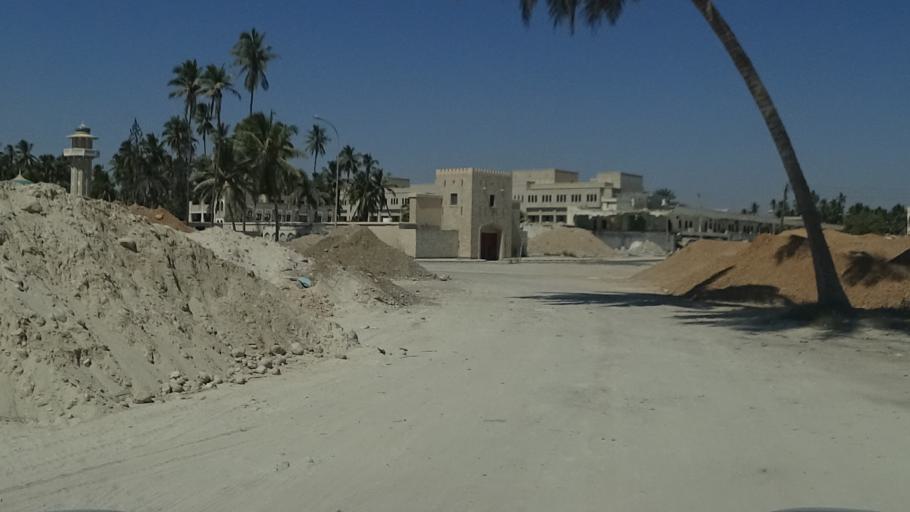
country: OM
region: Zufar
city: Salalah
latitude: 16.9998
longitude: 54.1018
